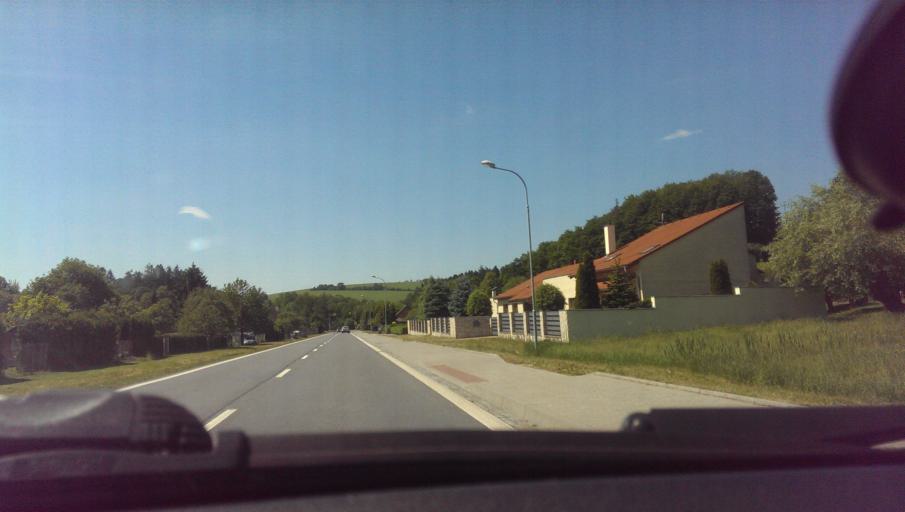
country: CZ
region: Zlin
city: Breznice
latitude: 49.1819
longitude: 17.6471
